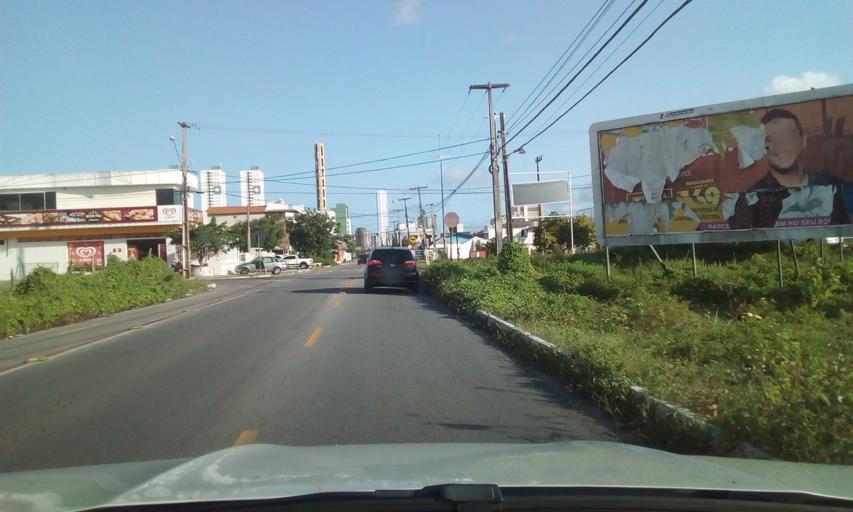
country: BR
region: Paraiba
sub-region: Joao Pessoa
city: Joao Pessoa
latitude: -7.0675
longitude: -34.8436
